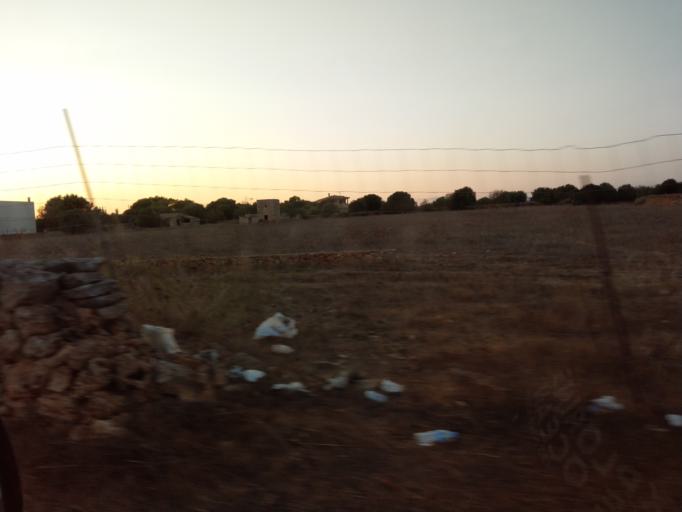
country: ES
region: Balearic Islands
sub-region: Illes Balears
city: Ses Salines
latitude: 39.3350
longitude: 3.0424
